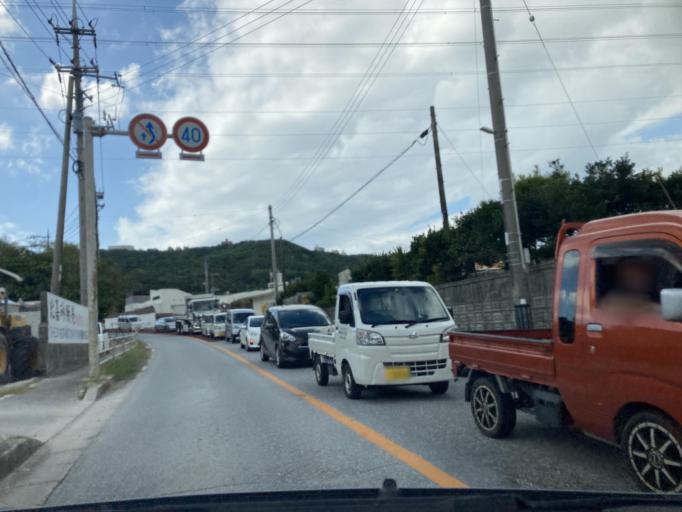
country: JP
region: Okinawa
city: Ginowan
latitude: 26.2540
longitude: 127.7842
